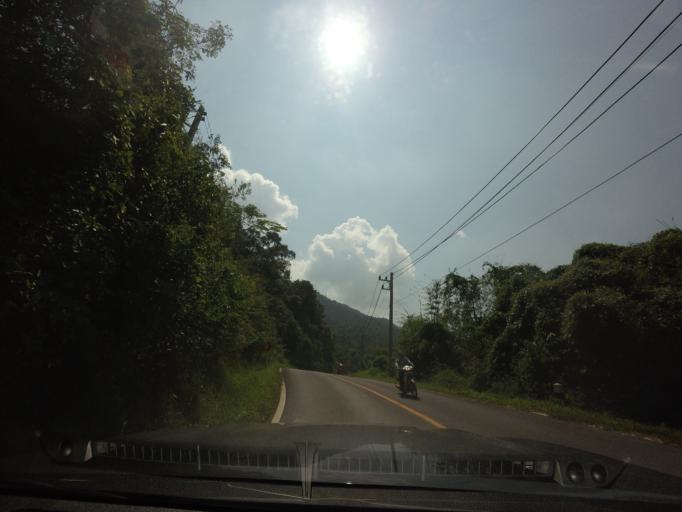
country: TH
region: Nan
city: Bo Kluea
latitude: 19.1300
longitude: 101.1495
